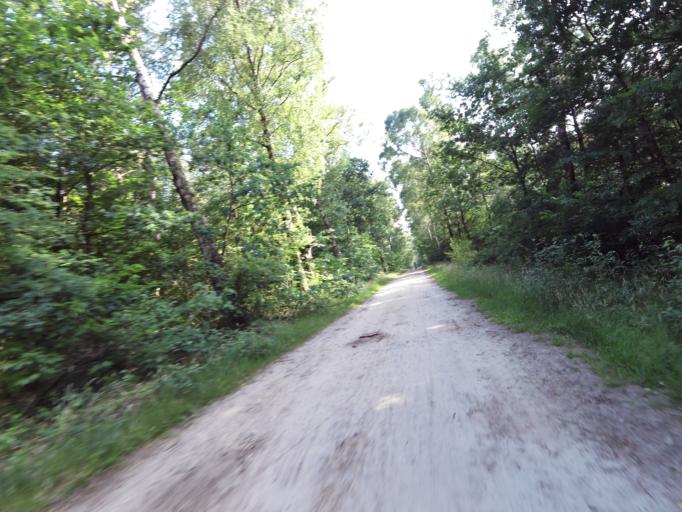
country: DE
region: Lower Saxony
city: Nordholz
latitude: 53.8459
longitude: 8.5921
